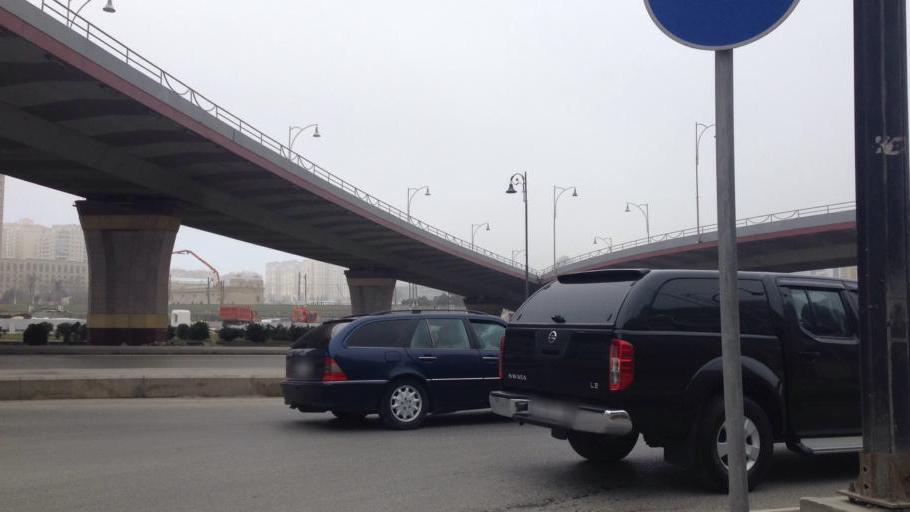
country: AZ
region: Baki
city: Baku
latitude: 40.3884
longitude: 49.8664
